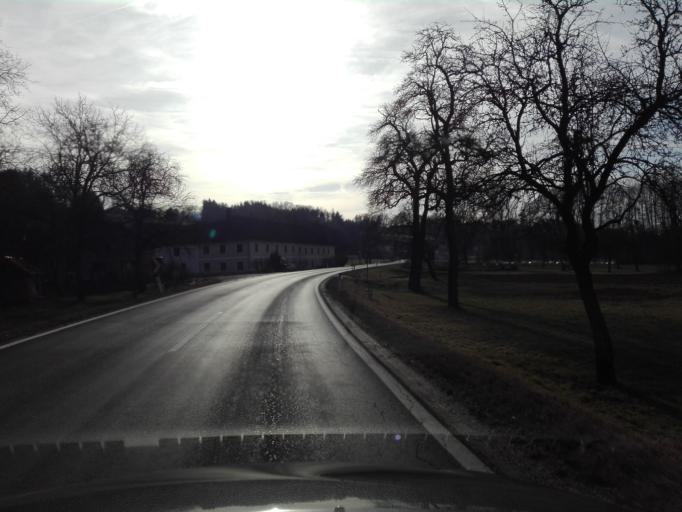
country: AT
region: Lower Austria
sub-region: Politischer Bezirk Amstetten
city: Amstetten
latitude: 48.1877
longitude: 14.8441
